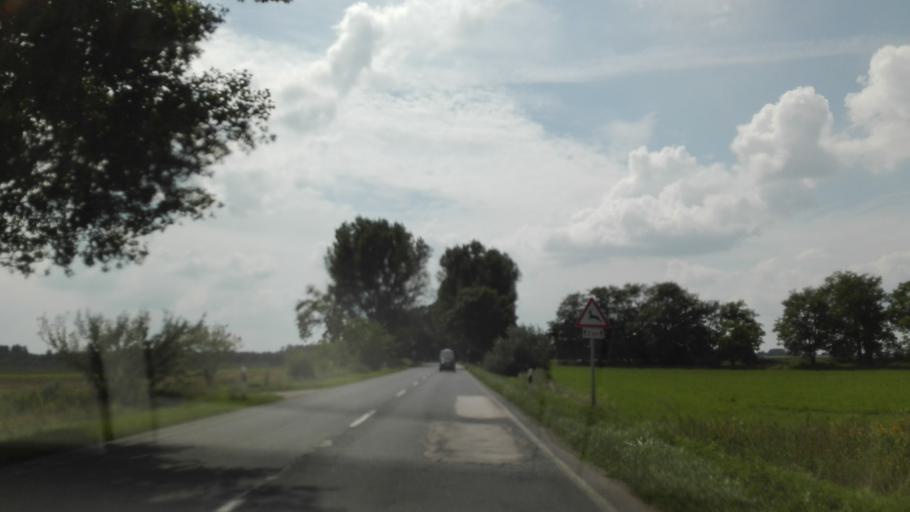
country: HU
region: Fejer
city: Alap
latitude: 46.7865
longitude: 18.6868
